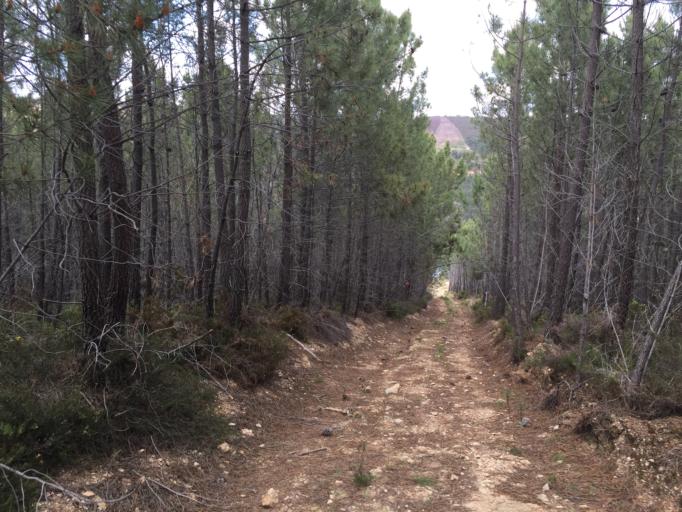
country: PT
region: Coimbra
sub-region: Pampilhosa da Serra
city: Pampilhosa da Serra
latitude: 40.1078
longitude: -7.8672
